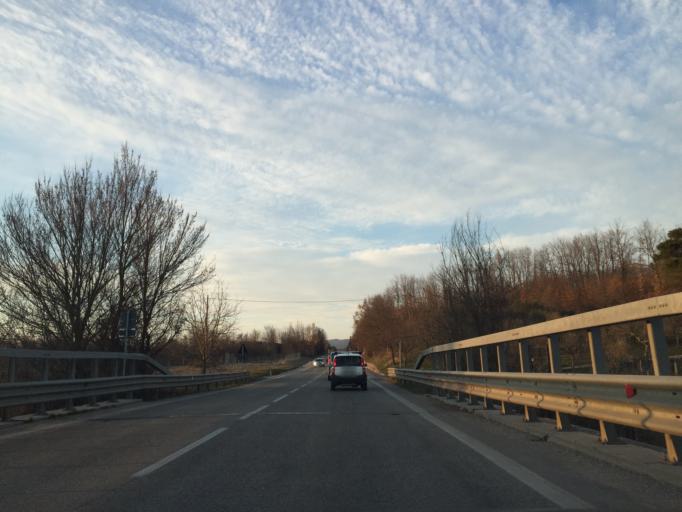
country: IT
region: Molise
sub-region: Provincia di Campobasso
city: Vinchiaturo
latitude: 41.4966
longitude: 14.6094
